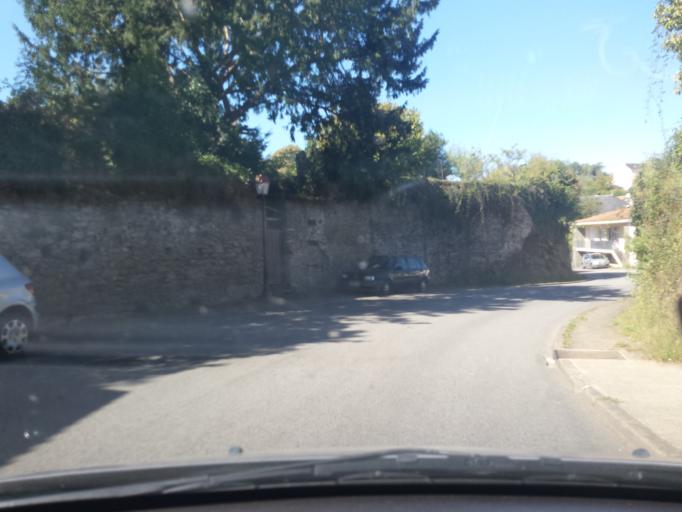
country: FR
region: Pays de la Loire
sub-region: Departement de la Vendee
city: Apremont
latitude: 46.7491
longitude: -1.7395
